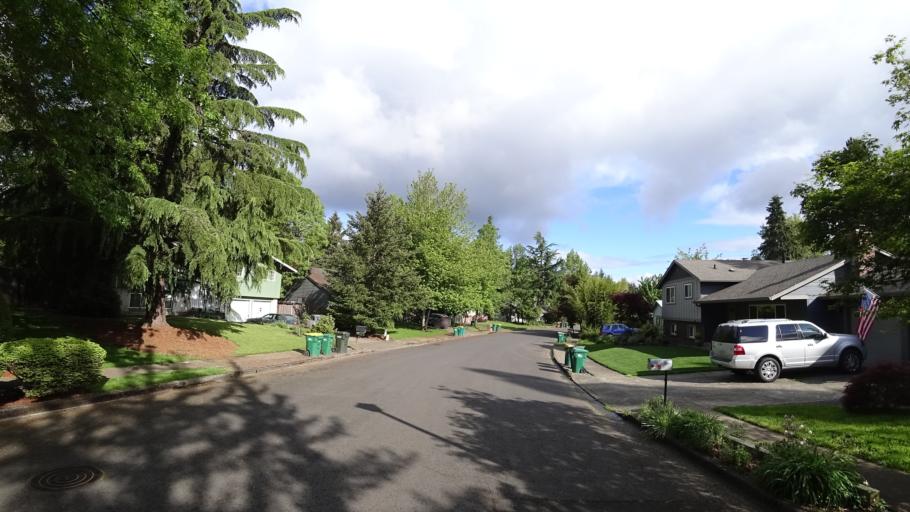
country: US
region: Oregon
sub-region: Washington County
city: Beaverton
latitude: 45.4643
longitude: -122.8251
